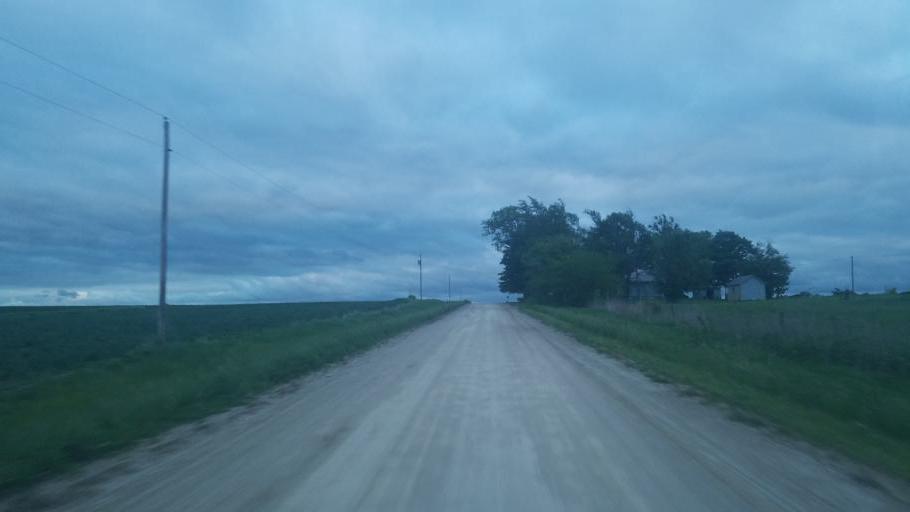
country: US
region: Iowa
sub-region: Decatur County
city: Lamoni
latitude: 40.5947
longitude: -93.9458
